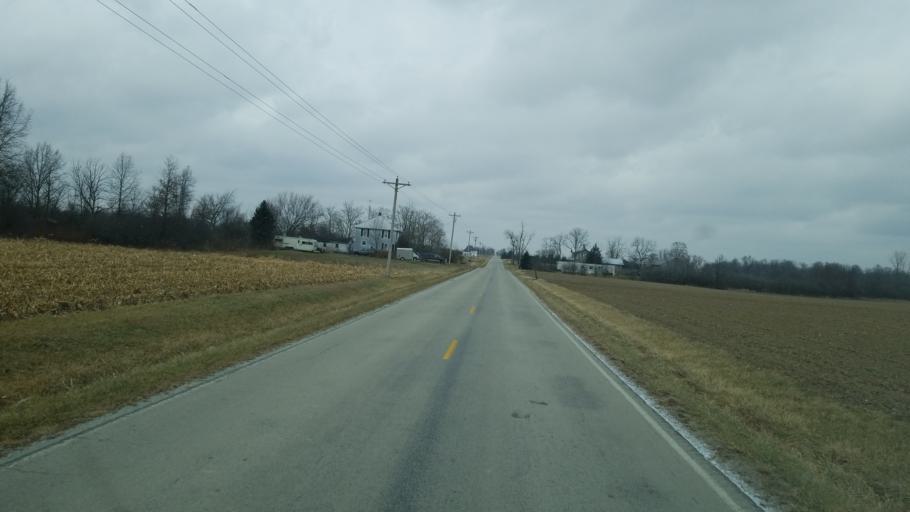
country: US
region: Ohio
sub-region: Hardin County
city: Forest
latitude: 40.7768
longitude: -83.4195
